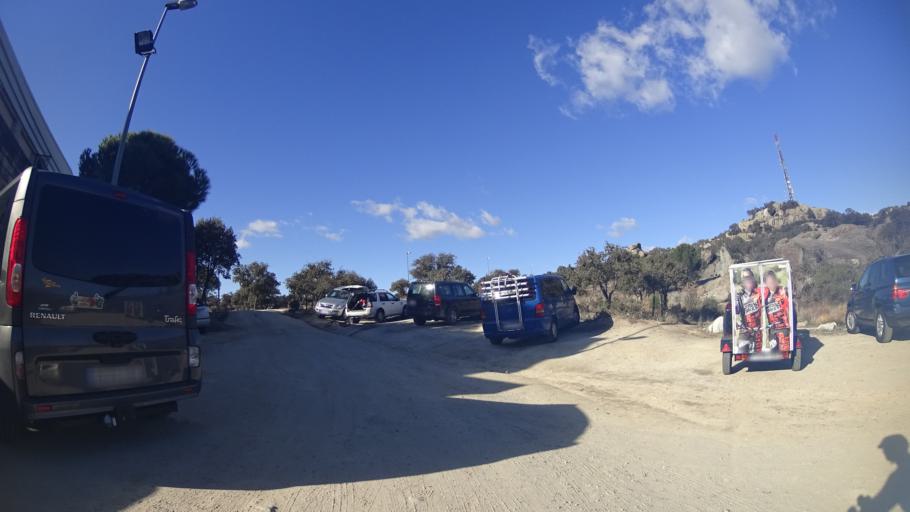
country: ES
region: Madrid
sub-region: Provincia de Madrid
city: Torrelodones
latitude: 40.5800
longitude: -3.9390
